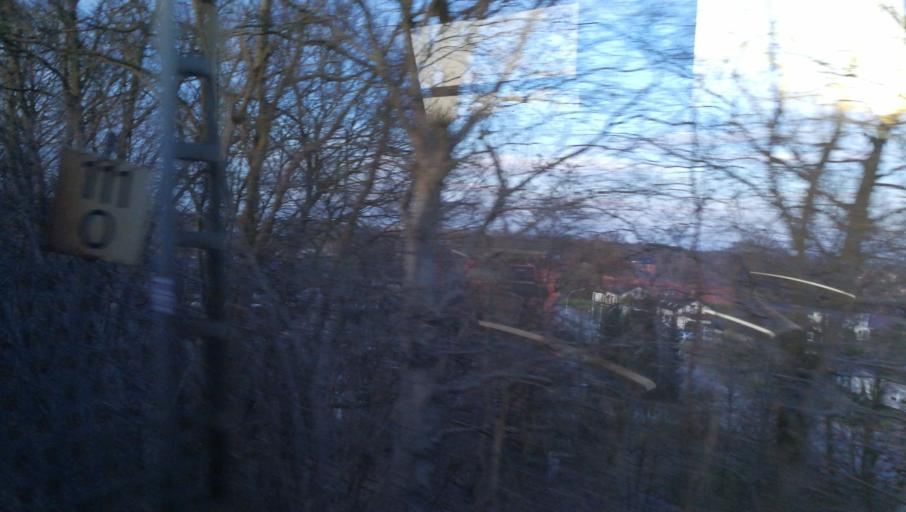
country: DE
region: Schleswig-Holstein
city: Schacht-Audorf
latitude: 54.3052
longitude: 9.7030
